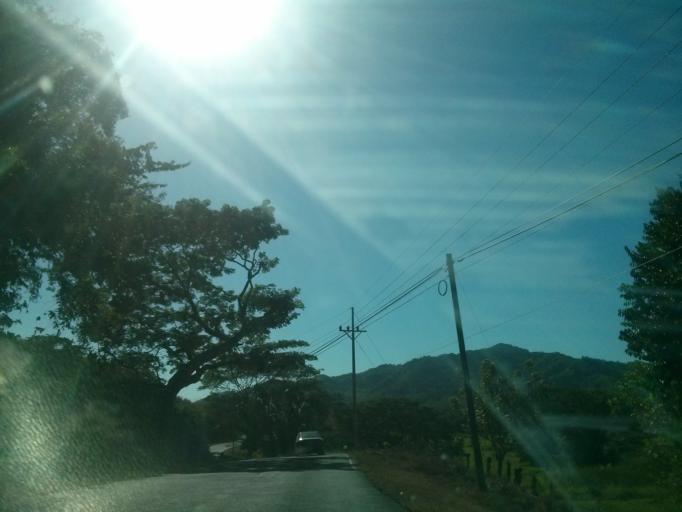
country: CR
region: Puntarenas
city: Paquera
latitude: 9.7665
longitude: -84.9783
